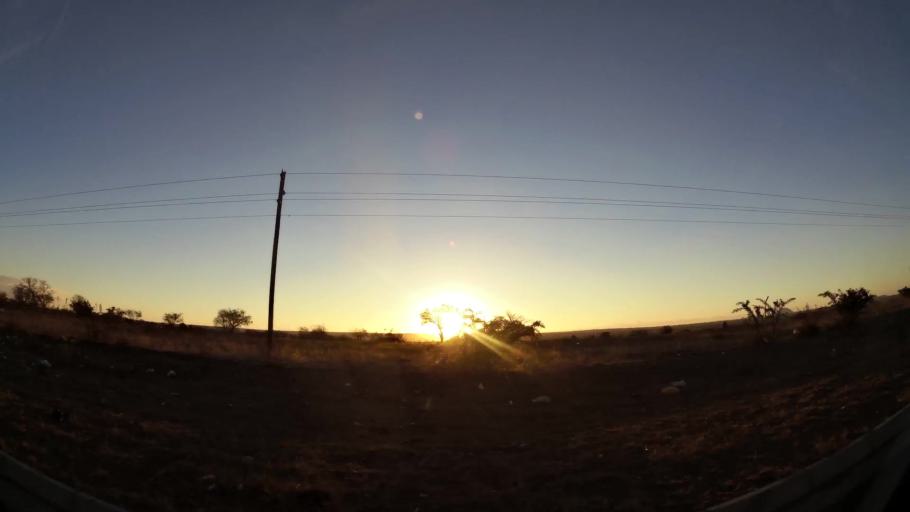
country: ZA
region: Limpopo
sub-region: Capricorn District Municipality
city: Polokwane
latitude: -23.8610
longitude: 29.3742
